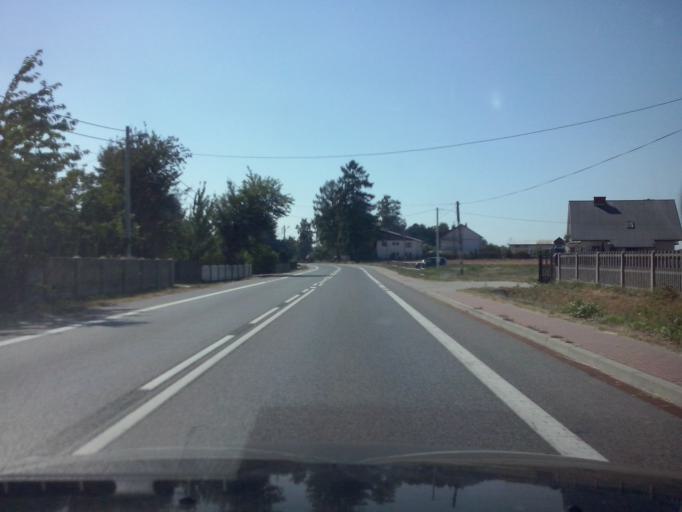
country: PL
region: Swietokrzyskie
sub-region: Powiat kielecki
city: Wola Jachowa
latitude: 50.8520
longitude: 20.8821
